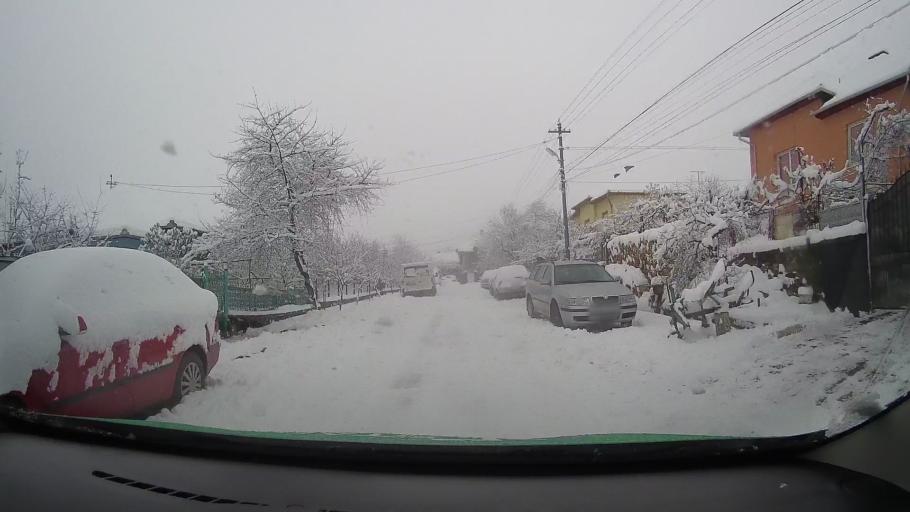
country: RO
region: Hunedoara
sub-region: Comuna Teliucu Inferior
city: Teliucu Inferior
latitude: 45.7001
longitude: 22.8938
